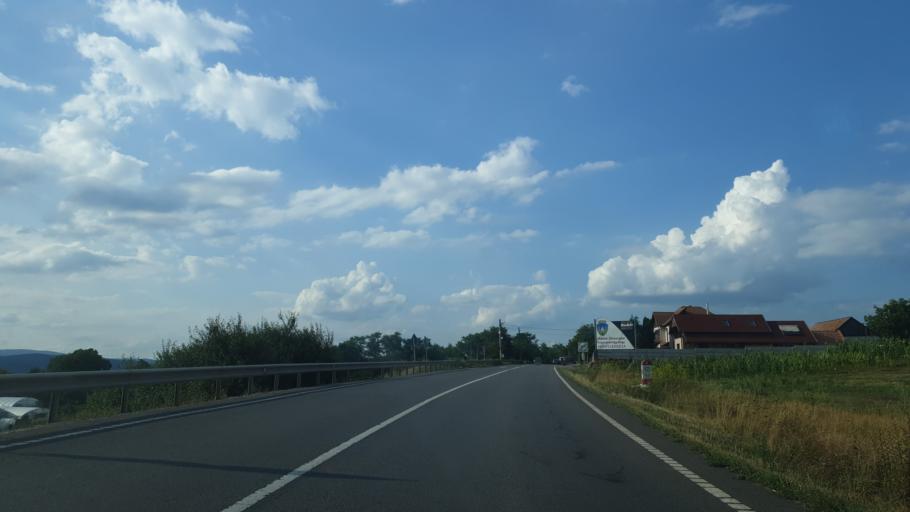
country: RO
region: Covasna
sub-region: Comuna Chichis
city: Chichis
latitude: 45.8087
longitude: 25.8005
